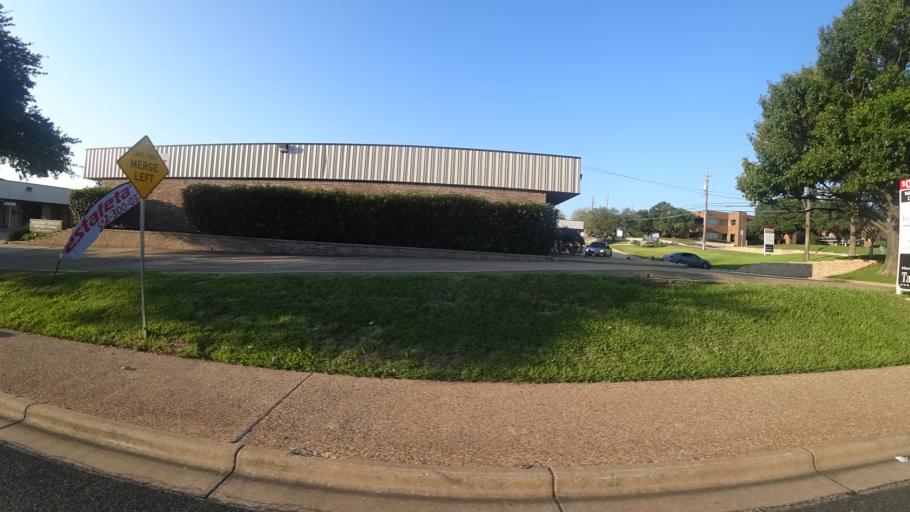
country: US
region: Texas
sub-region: Travis County
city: Austin
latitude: 30.3371
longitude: -97.6829
